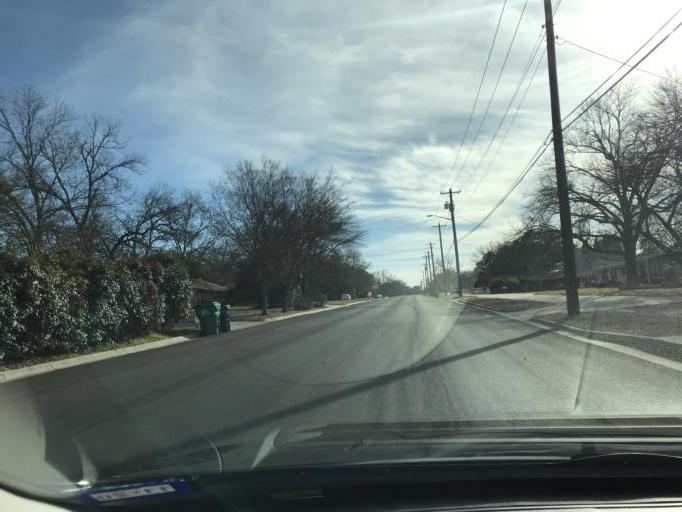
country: US
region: Texas
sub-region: Denton County
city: Denton
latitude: 33.2230
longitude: -97.1551
